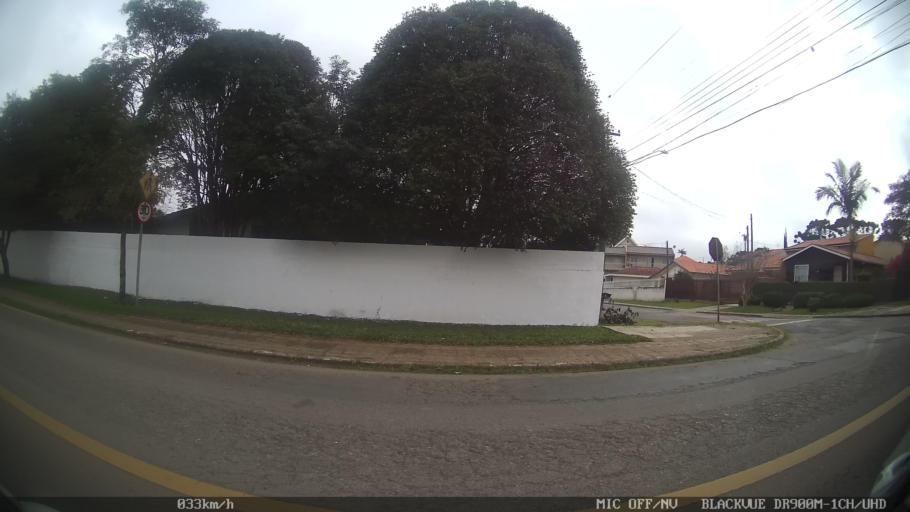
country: BR
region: Parana
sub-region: Almirante Tamandare
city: Almirante Tamandare
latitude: -25.3662
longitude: -49.2640
